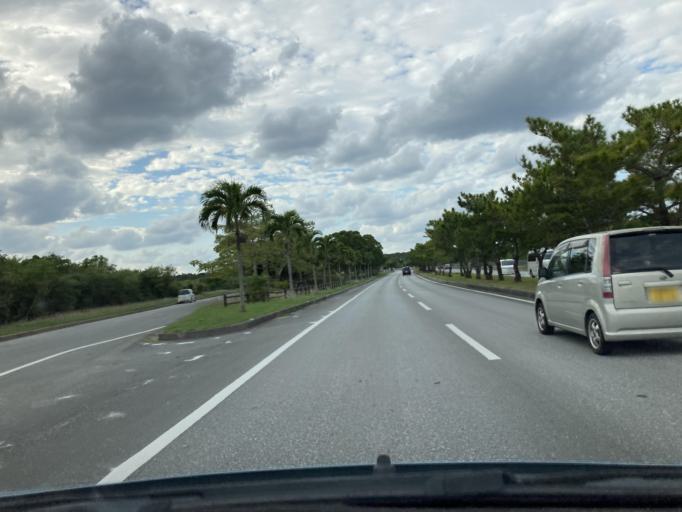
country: JP
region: Okinawa
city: Okinawa
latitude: 26.3665
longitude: 127.7874
